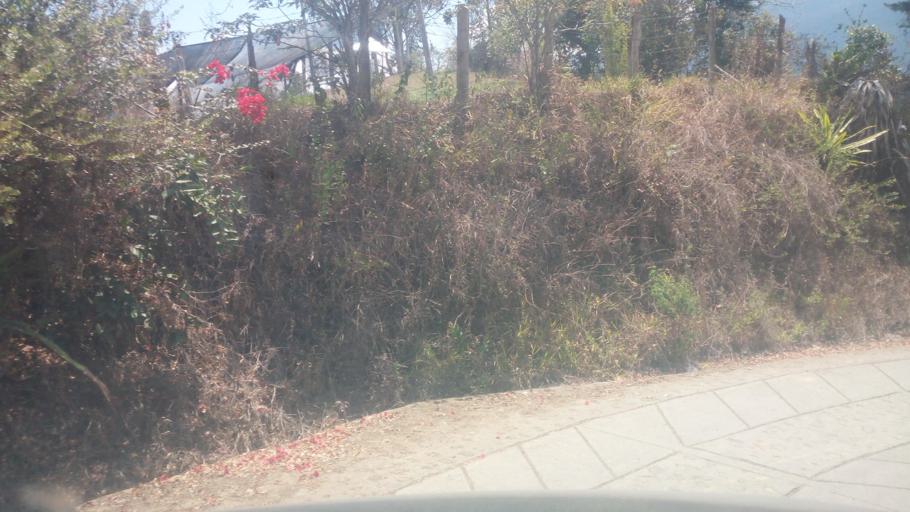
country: CO
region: Boyaca
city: Guateque
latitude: 4.9932
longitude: -73.4618
